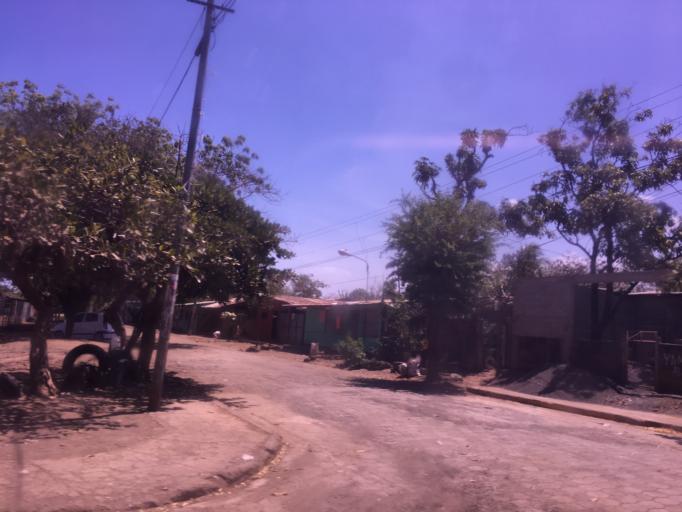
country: NI
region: Managua
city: Ciudad Sandino
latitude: 12.1605
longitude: -86.3603
